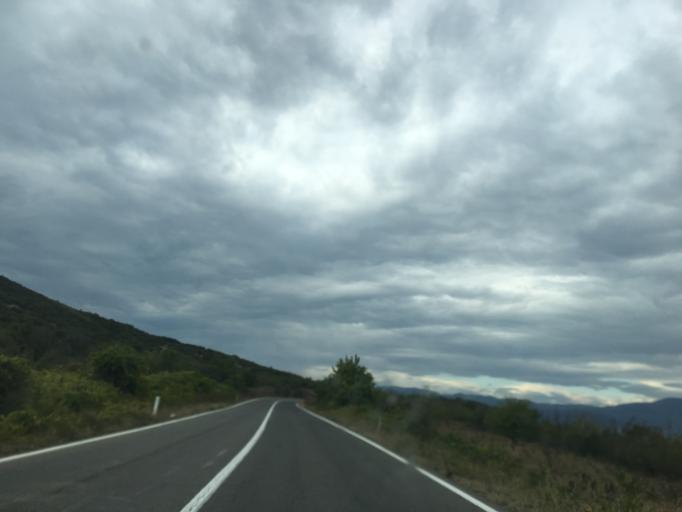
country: MK
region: Gevgelija
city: Miravci
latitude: 41.2715
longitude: 22.4780
